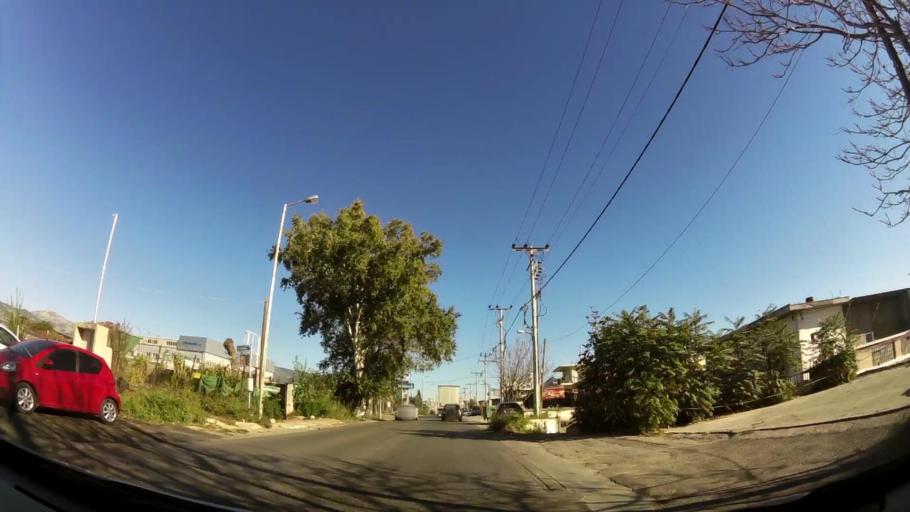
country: GR
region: Attica
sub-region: Nomarchia Athinas
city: Metamorfosi
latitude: 38.0811
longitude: 23.7628
